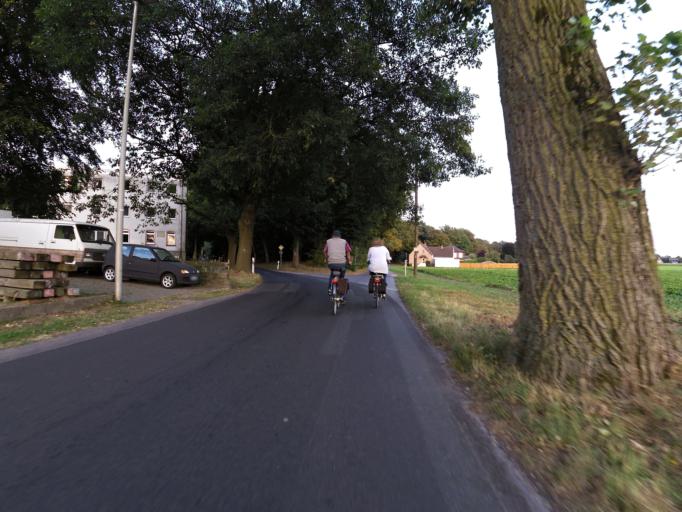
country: DE
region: North Rhine-Westphalia
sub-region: Regierungsbezirk Dusseldorf
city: Emmerich
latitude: 51.8540
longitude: 6.2105
